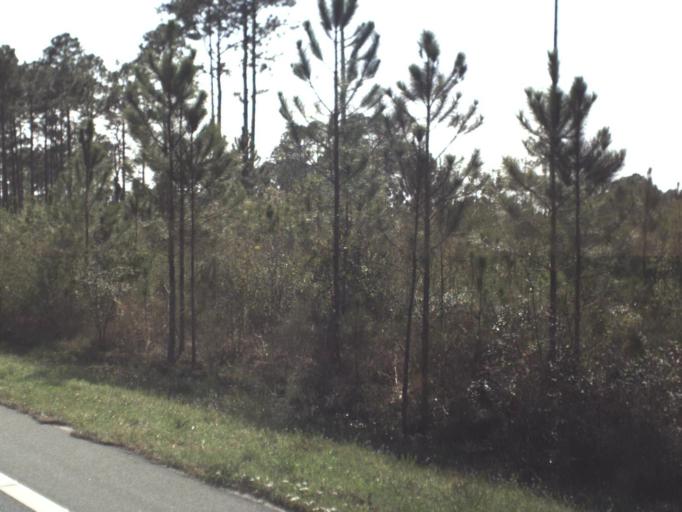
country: US
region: Florida
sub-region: Wakulla County
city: Crawfordville
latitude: 30.0299
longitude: -84.4980
